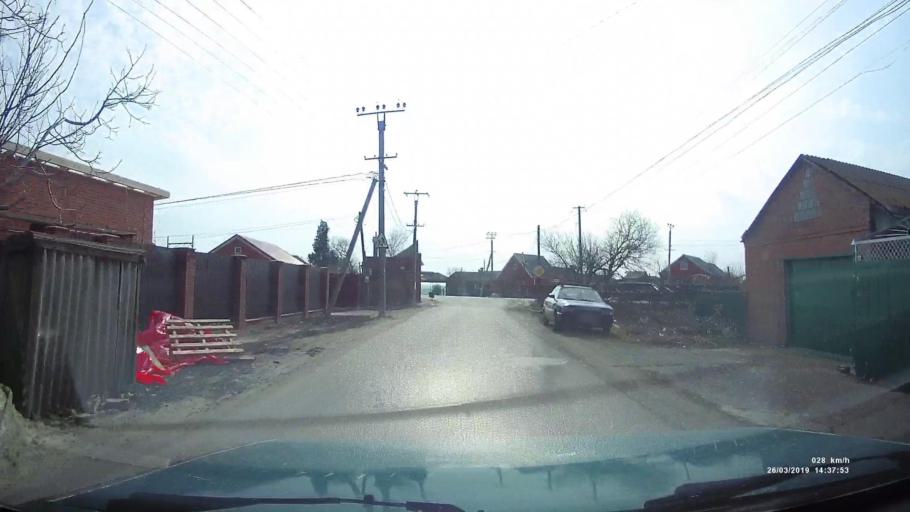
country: RU
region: Rostov
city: Novobessergenovka
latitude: 47.1832
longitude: 38.8646
